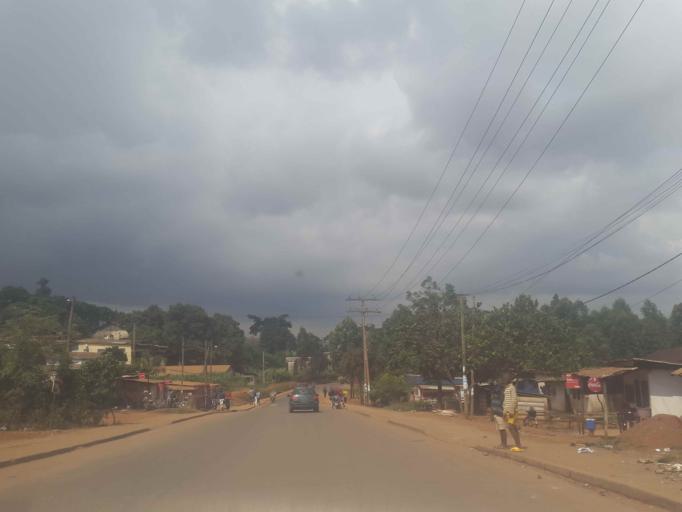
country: CM
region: Centre
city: Yaounde
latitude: 3.8716
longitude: 11.4817
